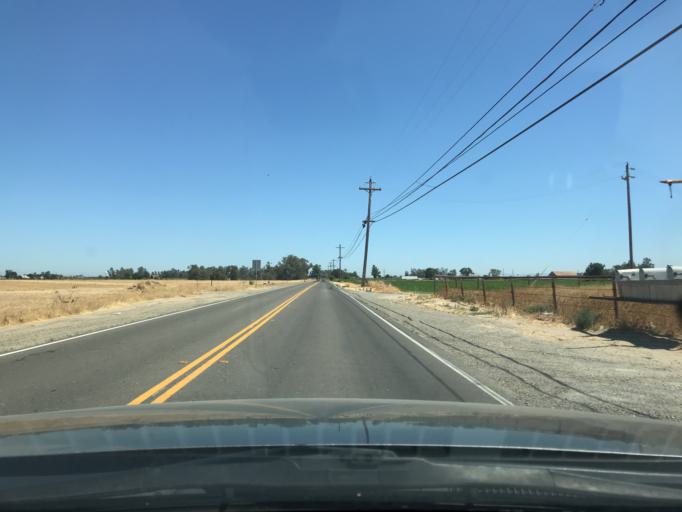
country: US
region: California
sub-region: Merced County
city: Atwater
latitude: 37.3319
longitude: -120.5589
